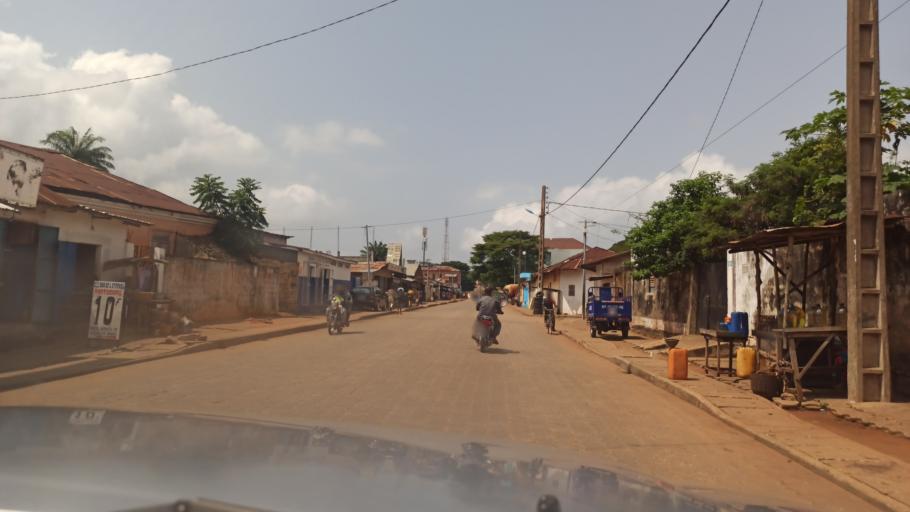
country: BJ
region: Queme
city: Porto-Novo
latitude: 6.4769
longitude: 2.6217
